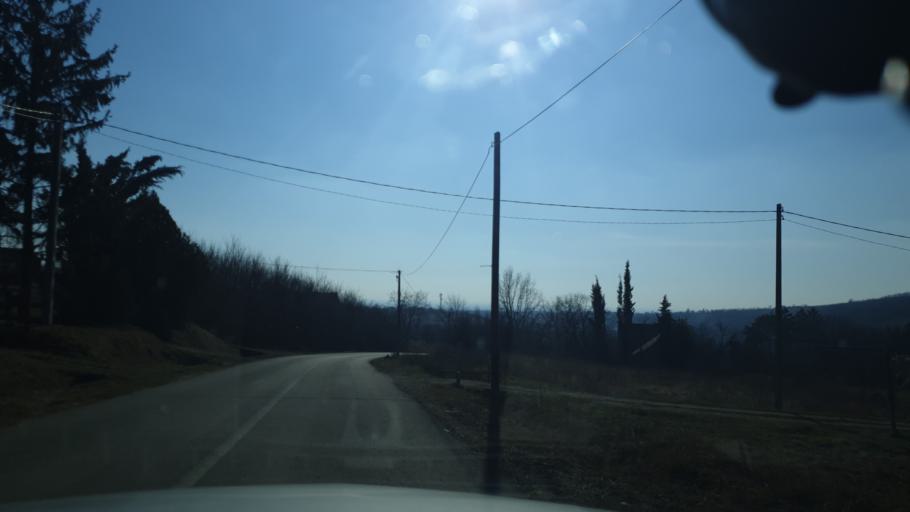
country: RS
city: Vrdnik
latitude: 45.1162
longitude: 19.7744
